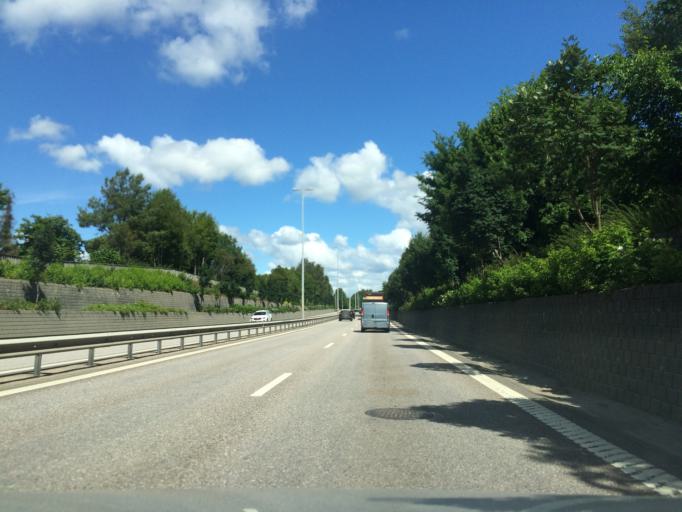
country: SE
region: Vaestra Goetaland
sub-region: Trollhattan
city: Trollhattan
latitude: 58.2912
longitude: 12.3100
